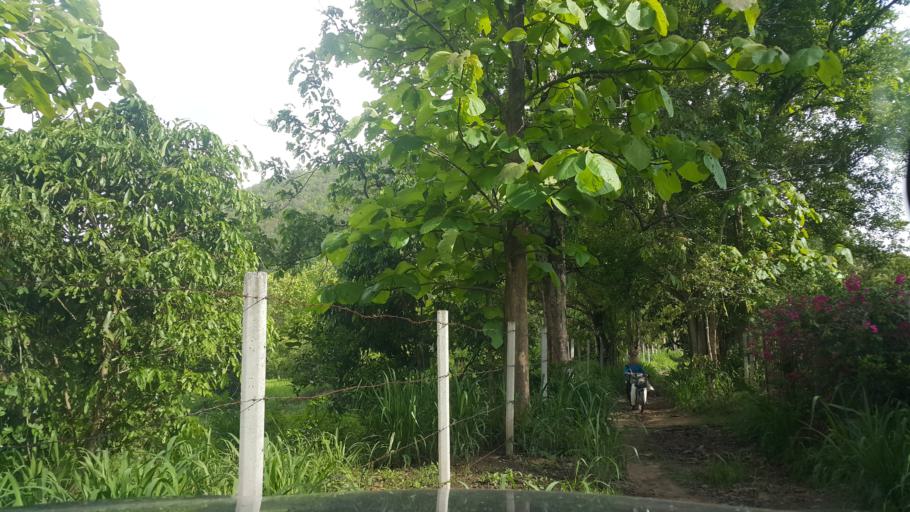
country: TH
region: Chiang Mai
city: Mae On
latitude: 18.7098
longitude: 99.2157
